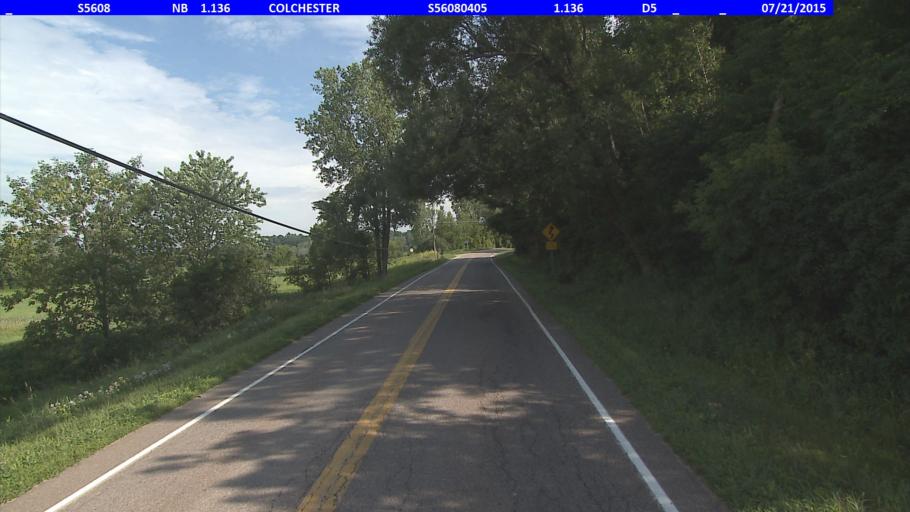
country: US
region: Vermont
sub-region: Chittenden County
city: Winooski
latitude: 44.5153
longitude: -73.2029
